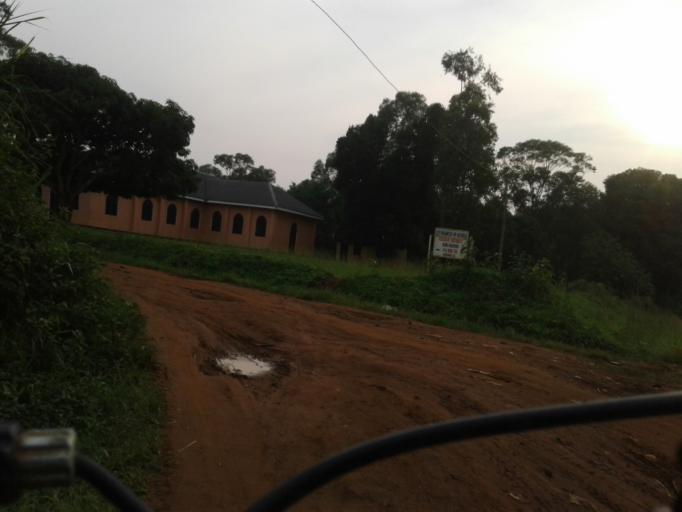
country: UG
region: Western Region
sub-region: Hoima District
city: Hoima
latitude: 1.4234
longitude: 31.3230
